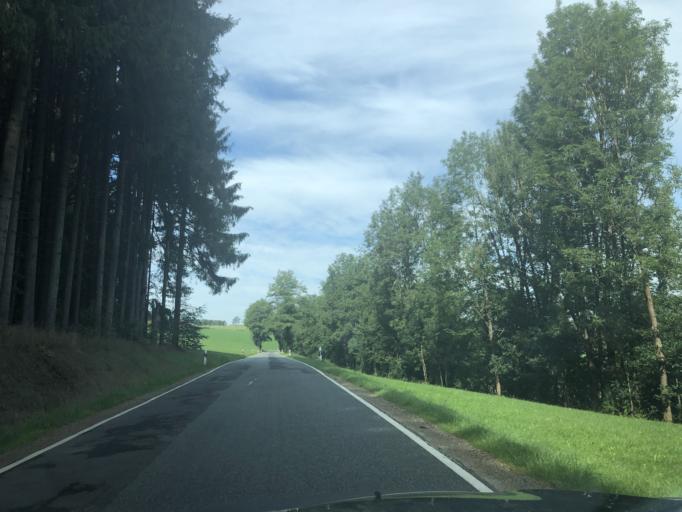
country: DE
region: Bavaria
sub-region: Upper Palatinate
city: Trabitz
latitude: 49.7785
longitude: 11.9108
